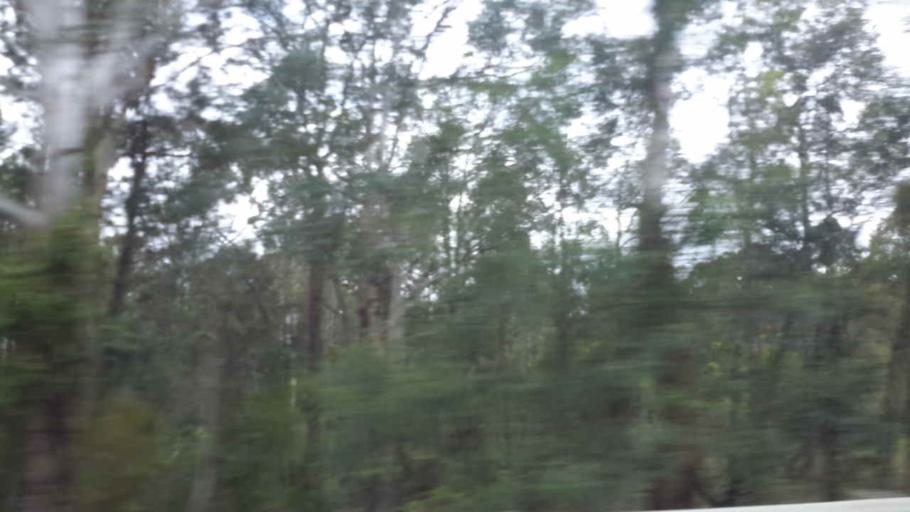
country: AU
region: New South Wales
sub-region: Hawkesbury
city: South Windsor
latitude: -33.6503
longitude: 150.7764
